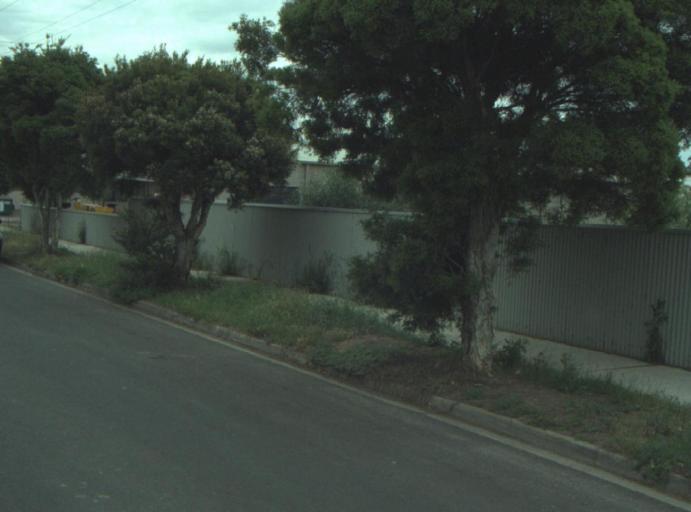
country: AU
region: Victoria
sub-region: Greater Geelong
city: Leopold
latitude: -38.1880
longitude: 144.4553
